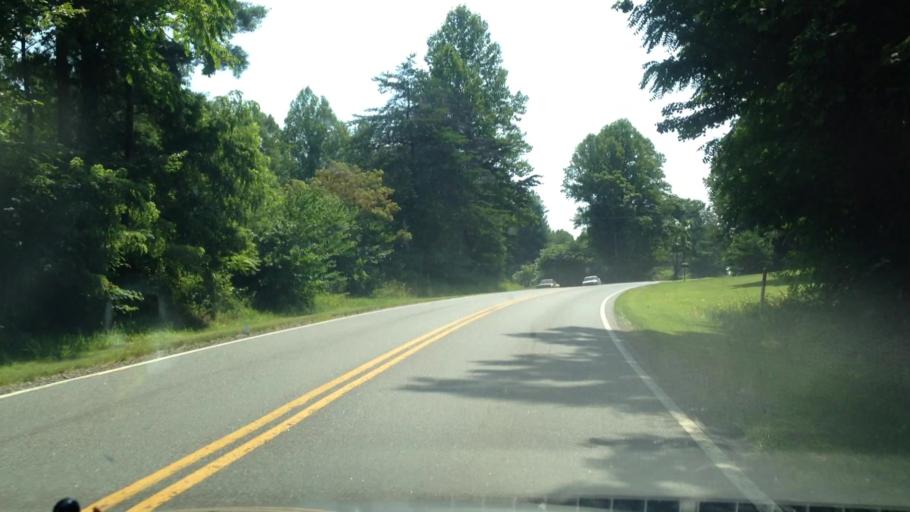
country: US
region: Virginia
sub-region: Patrick County
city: Stuart
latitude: 36.5872
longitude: -80.3982
